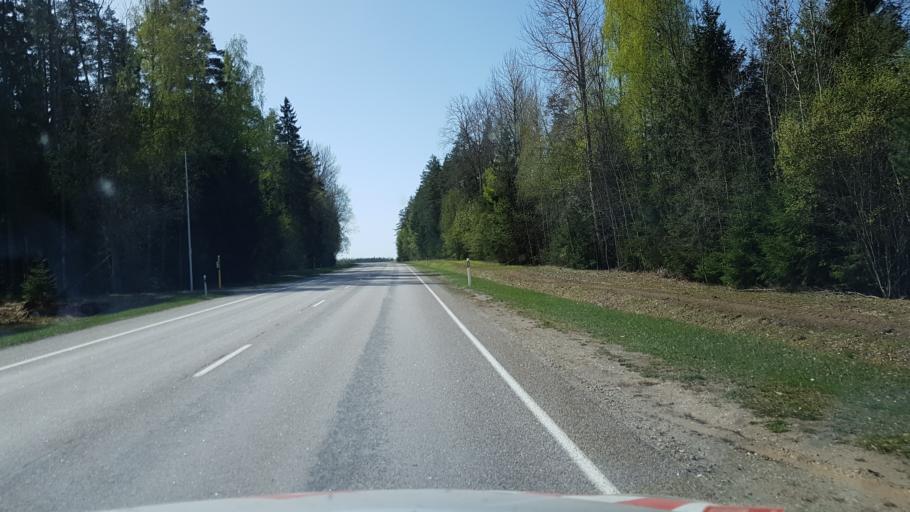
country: EE
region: Valgamaa
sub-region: Valga linn
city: Valga
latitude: 57.8467
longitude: 26.0584
